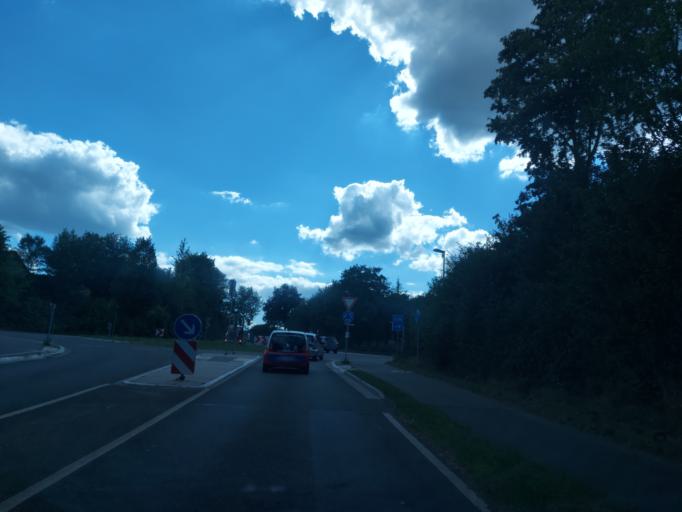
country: DE
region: Lower Saxony
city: Georgsmarienhutte
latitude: 52.2288
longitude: 8.0144
